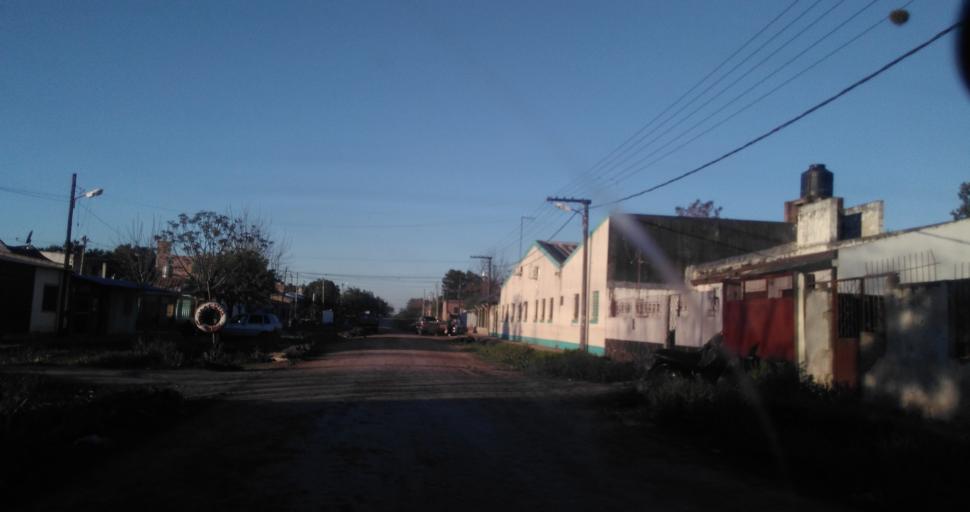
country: AR
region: Chaco
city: Fontana
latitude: -27.4255
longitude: -59.0244
